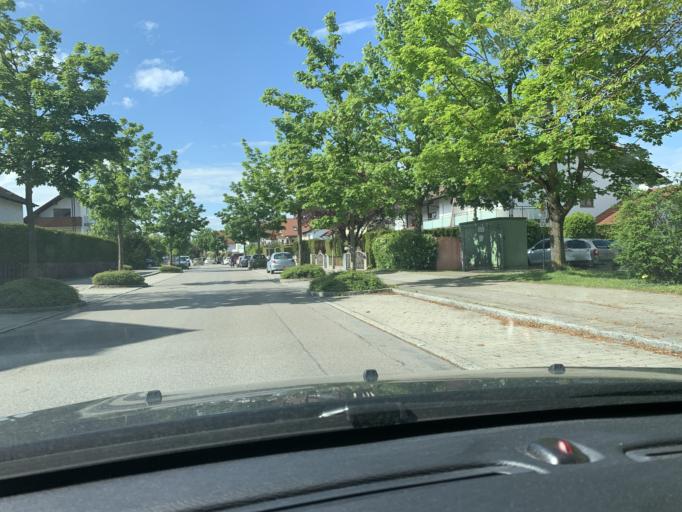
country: DE
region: Bavaria
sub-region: Upper Bavaria
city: Unterschleissheim
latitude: 48.2737
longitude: 11.5830
